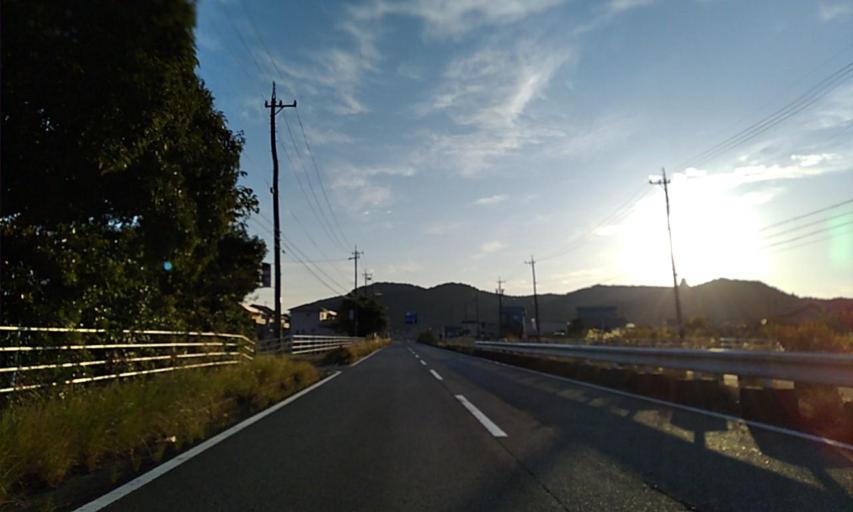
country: JP
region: Mie
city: Ise
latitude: 34.5048
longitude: 136.7699
